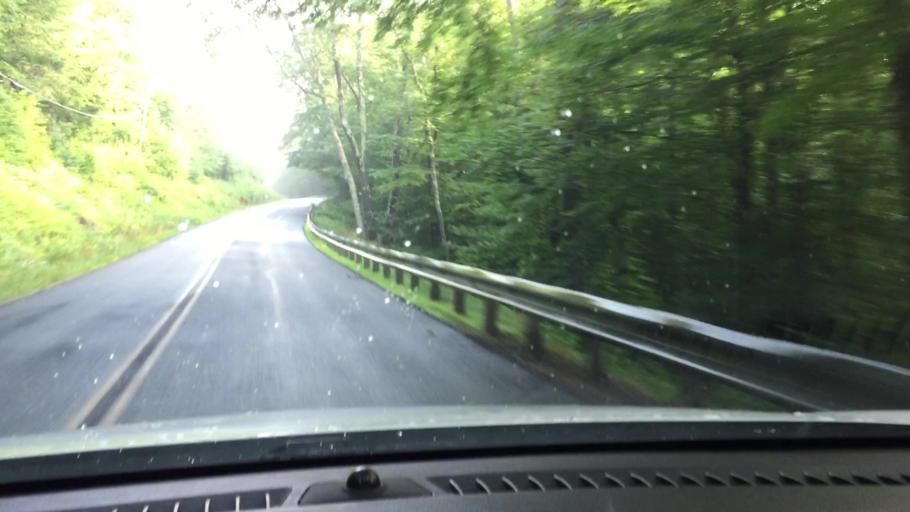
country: US
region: Massachusetts
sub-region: Berkshire County
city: Becket
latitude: 42.4051
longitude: -72.9793
